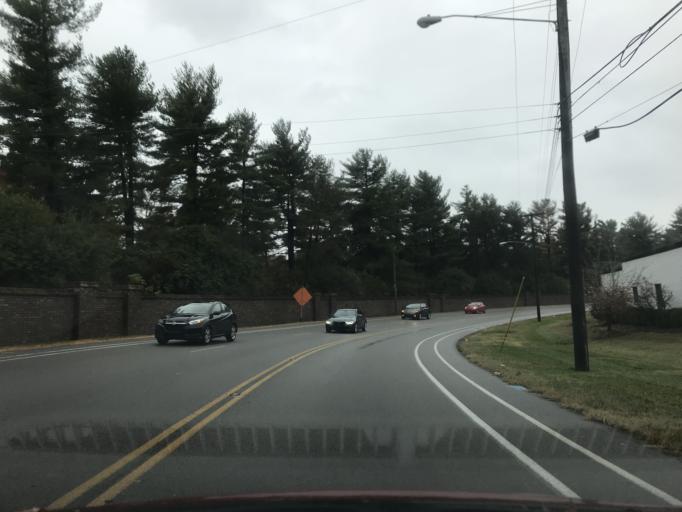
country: US
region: Indiana
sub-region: Clark County
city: Jeffersonville
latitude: 38.2456
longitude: -85.7062
